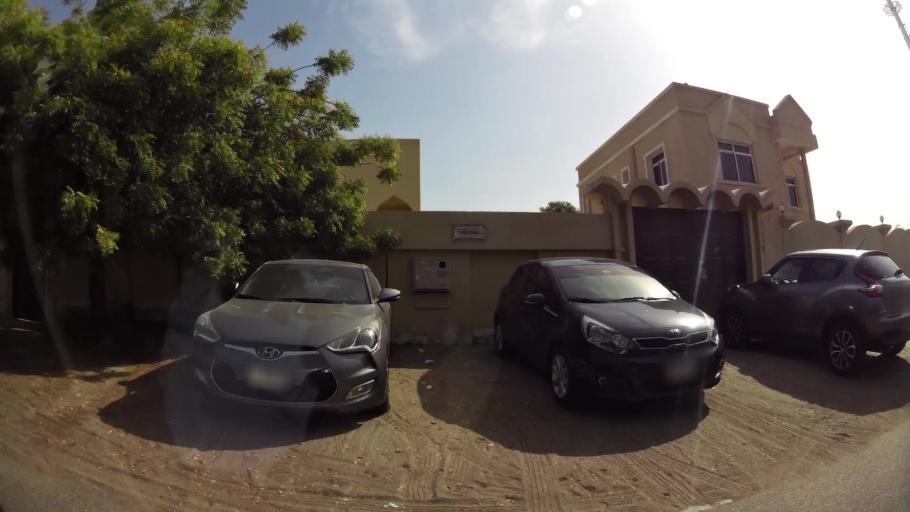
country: AE
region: Ash Shariqah
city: Sharjah
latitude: 25.2227
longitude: 55.3923
